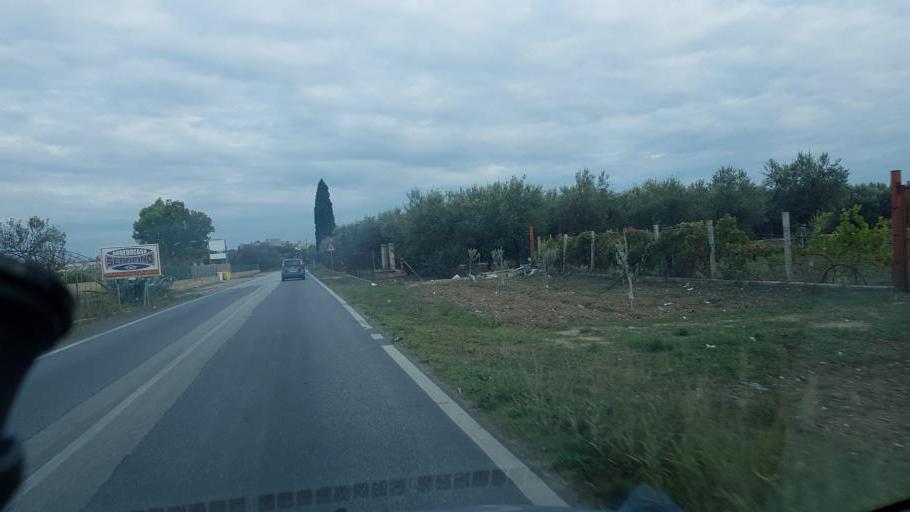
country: IT
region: Apulia
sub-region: Provincia di Brindisi
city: Oria
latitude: 40.5105
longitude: 17.6231
